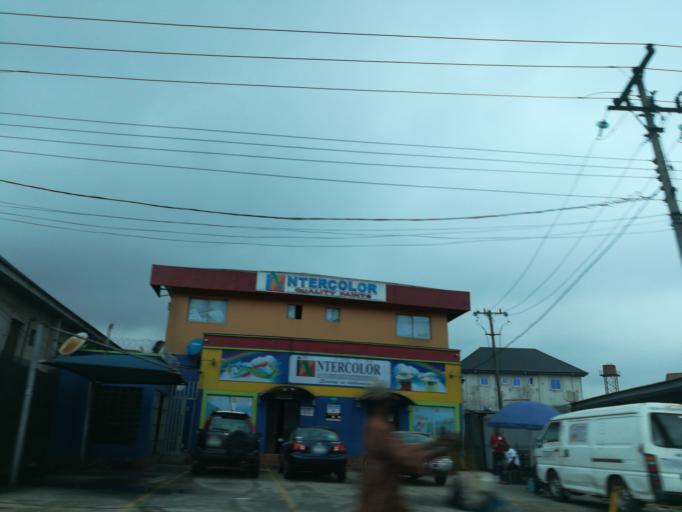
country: NG
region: Rivers
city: Port Harcourt
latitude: 4.8143
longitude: 7.0098
